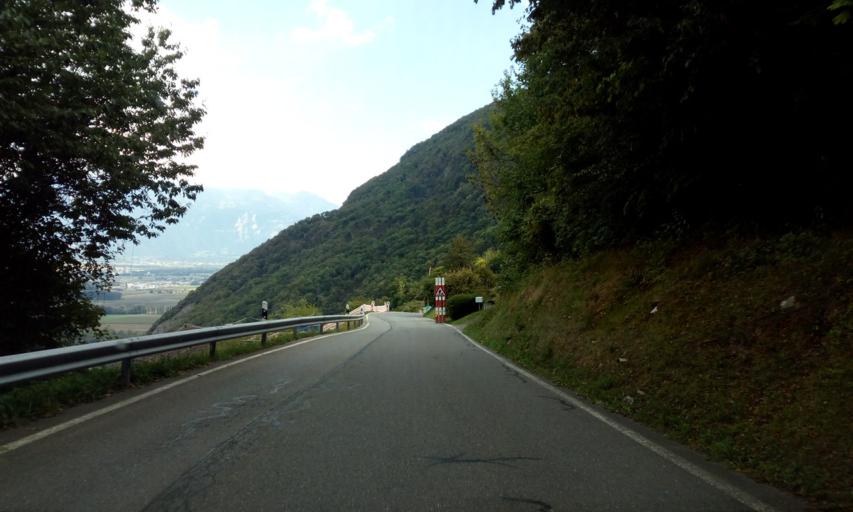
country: CH
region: Valais
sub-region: Monthey District
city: Vionnaz
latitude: 46.3097
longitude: 6.8923
